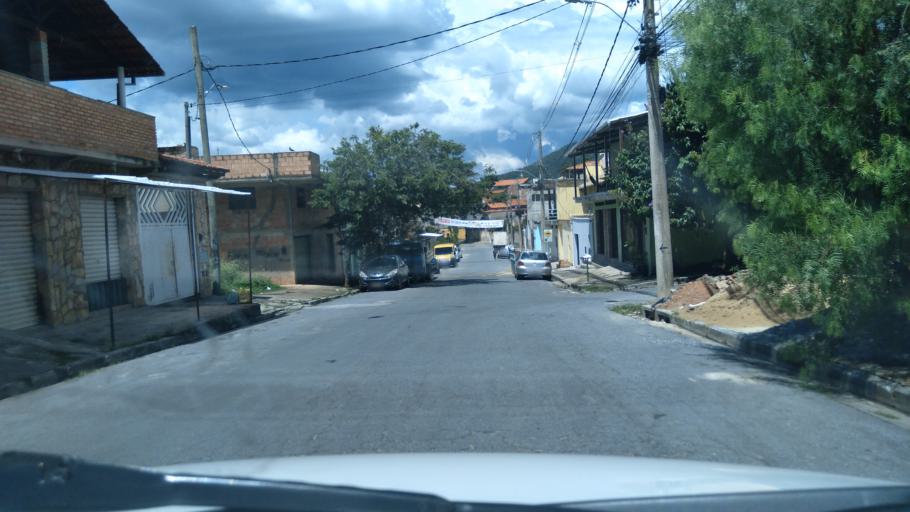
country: BR
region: Minas Gerais
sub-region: Belo Horizonte
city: Belo Horizonte
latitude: -19.8593
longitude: -43.8733
